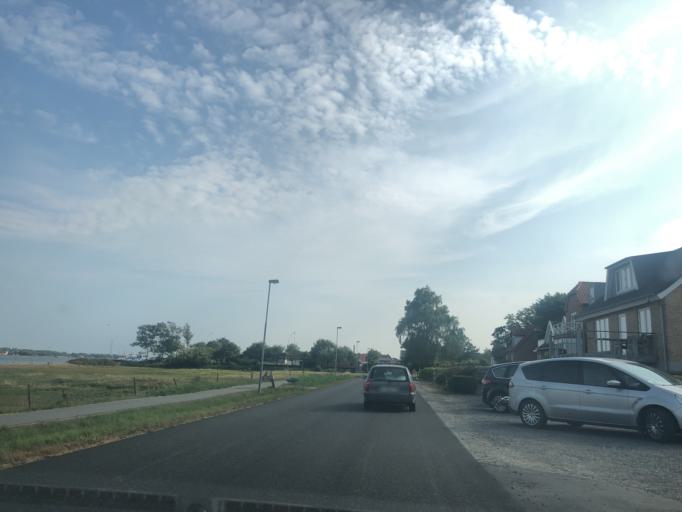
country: DK
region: North Denmark
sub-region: Morso Kommune
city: Nykobing Mors
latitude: 56.8089
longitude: 9.0208
